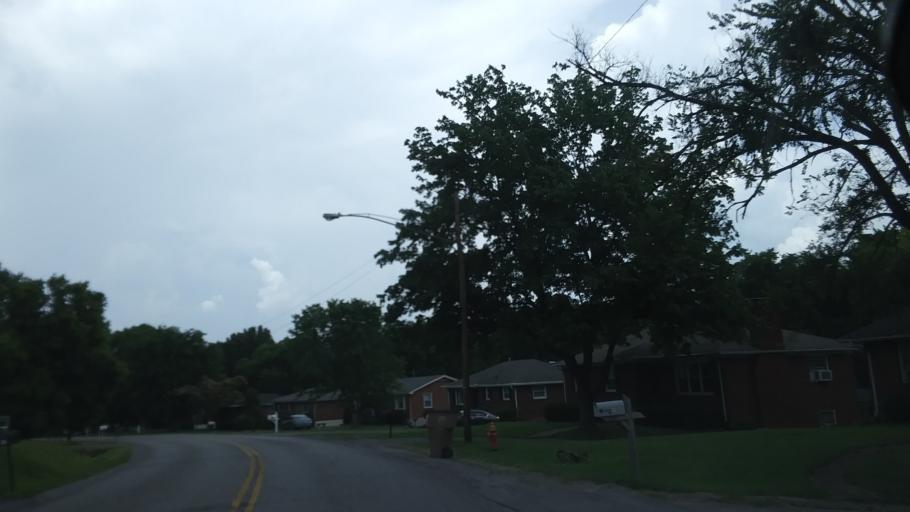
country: US
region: Tennessee
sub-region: Davidson County
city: Belle Meade
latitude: 36.1470
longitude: -86.8737
